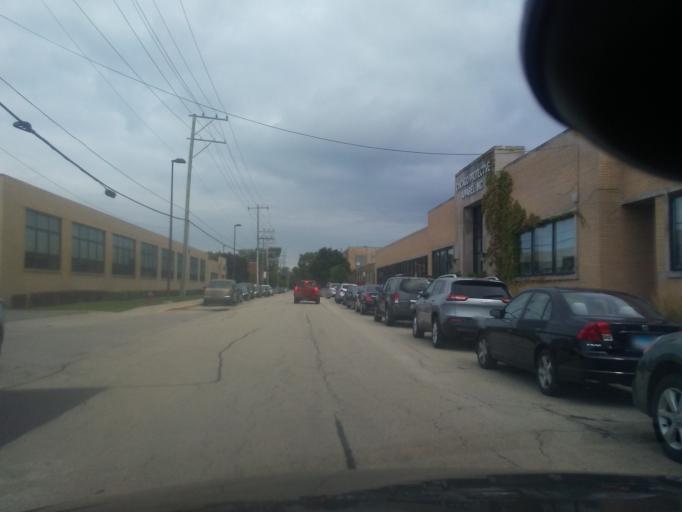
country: US
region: Illinois
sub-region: Cook County
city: Skokie
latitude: 42.0300
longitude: -87.7152
